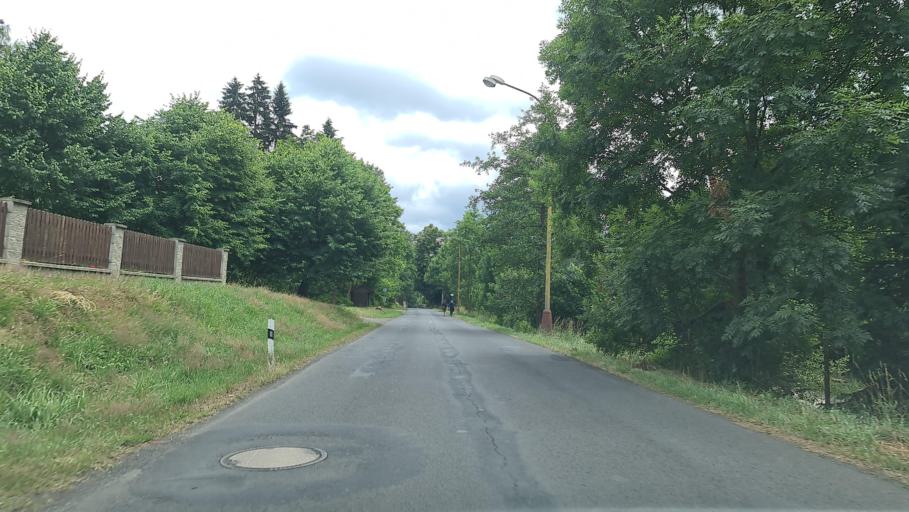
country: CZ
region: Karlovarsky
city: Kraslice
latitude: 50.3444
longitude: 12.5198
